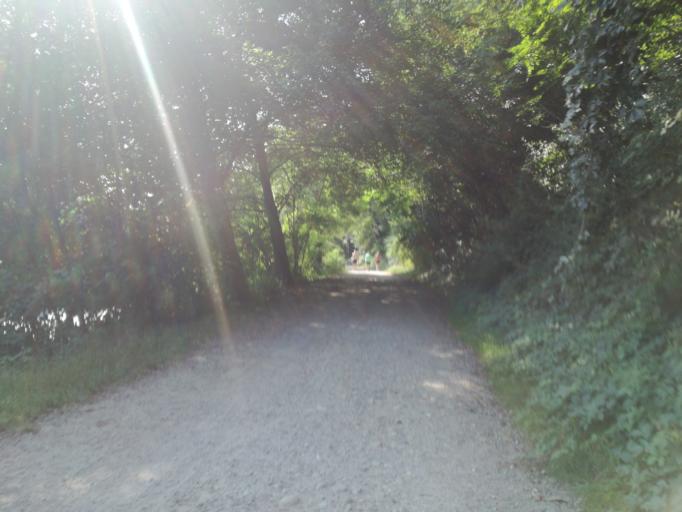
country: IT
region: Lombardy
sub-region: Citta metropolitana di Milano
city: Trezzo sull'Adda
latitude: 45.6135
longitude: 9.5164
